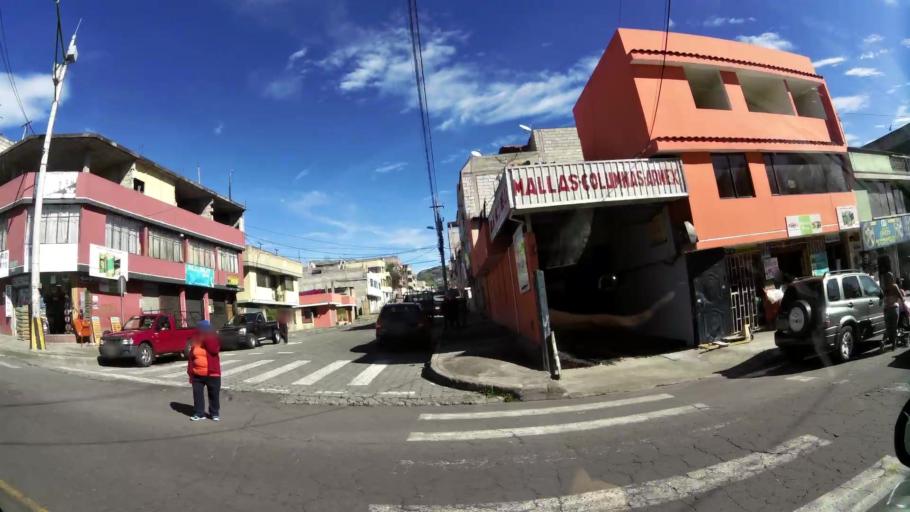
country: EC
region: Pichincha
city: Quito
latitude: -0.2953
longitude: -78.5634
